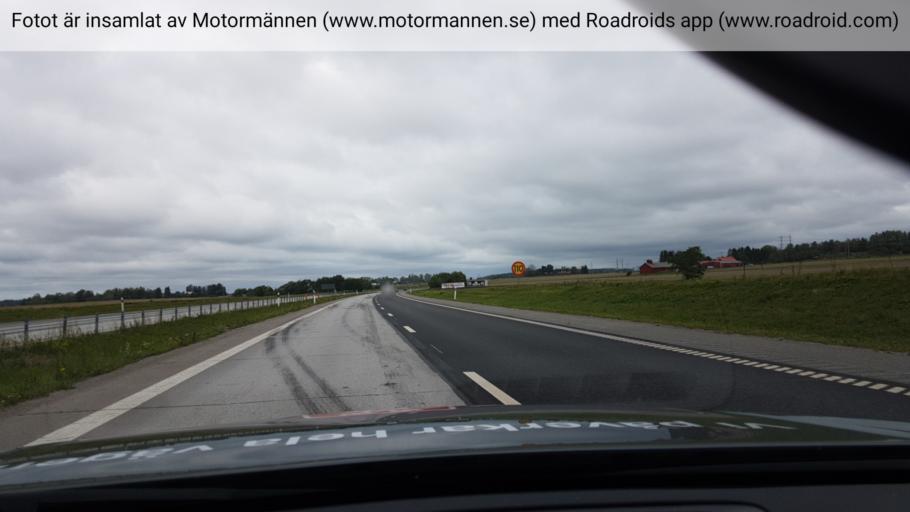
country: SE
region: Uppsala
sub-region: Uppsala Kommun
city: Gamla Uppsala
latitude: 59.8977
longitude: 17.6550
